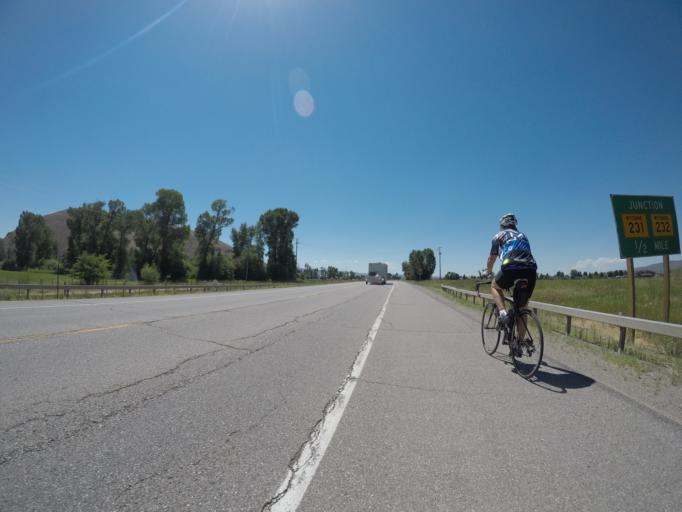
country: US
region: Idaho
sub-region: Bear Lake County
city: Montpelier
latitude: 42.0924
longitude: -110.9506
